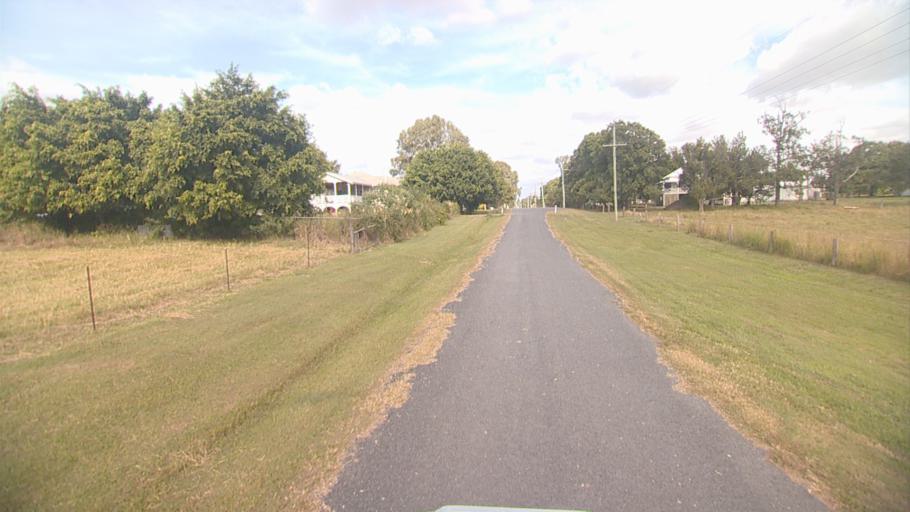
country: AU
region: Queensland
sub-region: Logan
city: Slacks Creek
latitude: -27.6767
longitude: 153.1595
